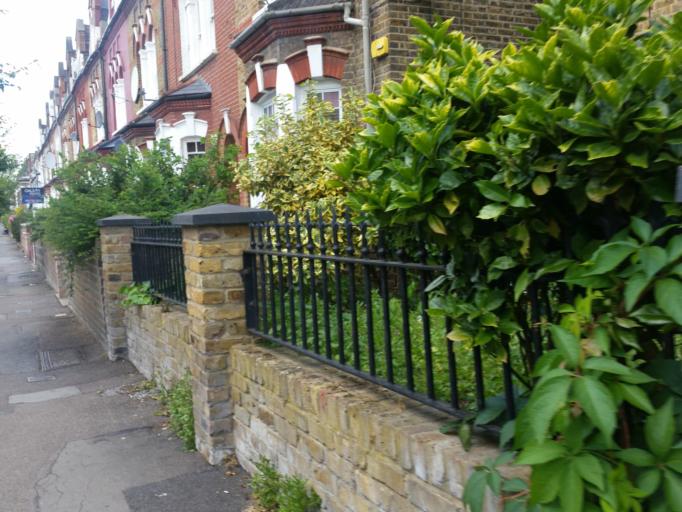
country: GB
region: England
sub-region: Greater London
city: Harringay
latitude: 51.5882
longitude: -0.1042
